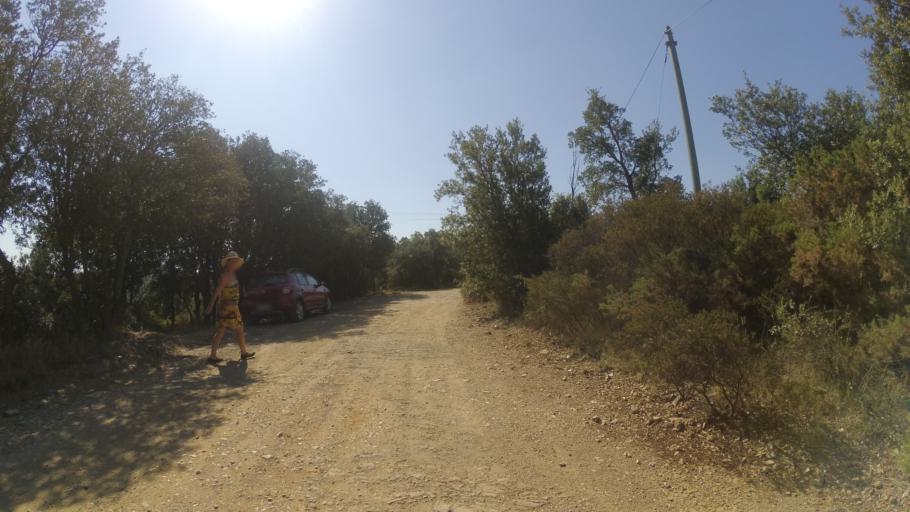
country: FR
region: Languedoc-Roussillon
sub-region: Departement des Pyrenees-Orientales
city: Ille-sur-Tet
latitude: 42.6172
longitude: 2.6769
